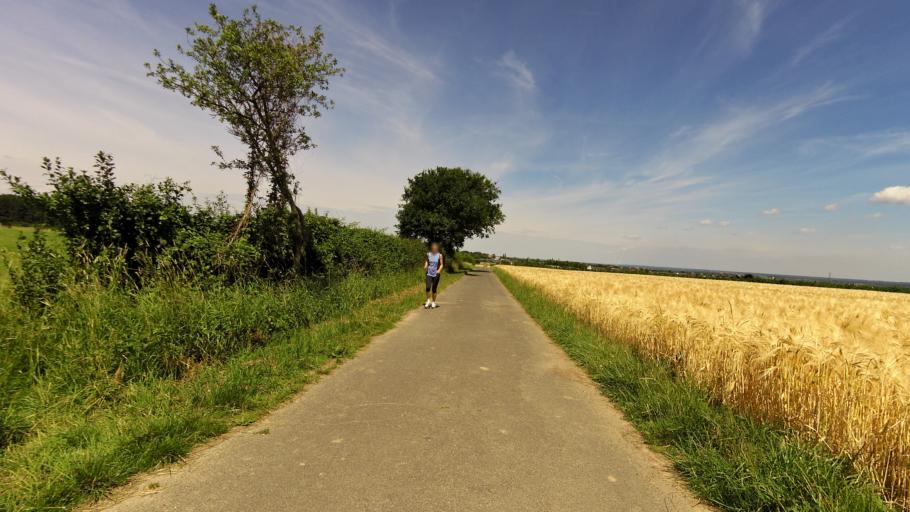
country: DE
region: North Rhine-Westphalia
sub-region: Regierungsbezirk Koln
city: Rheinbach
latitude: 50.6109
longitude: 6.9660
